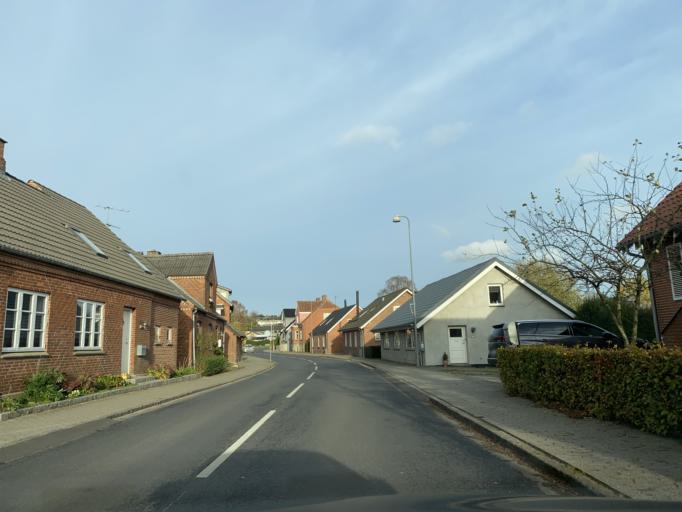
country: DK
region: Central Jutland
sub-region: Favrskov Kommune
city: Hammel
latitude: 56.2311
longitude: 9.7411
